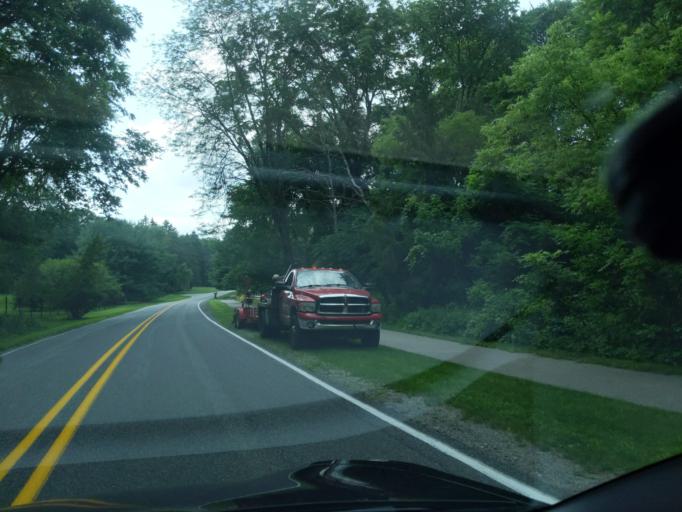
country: US
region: Michigan
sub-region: Kent County
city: Forest Hills
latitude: 42.9662
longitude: -85.5211
